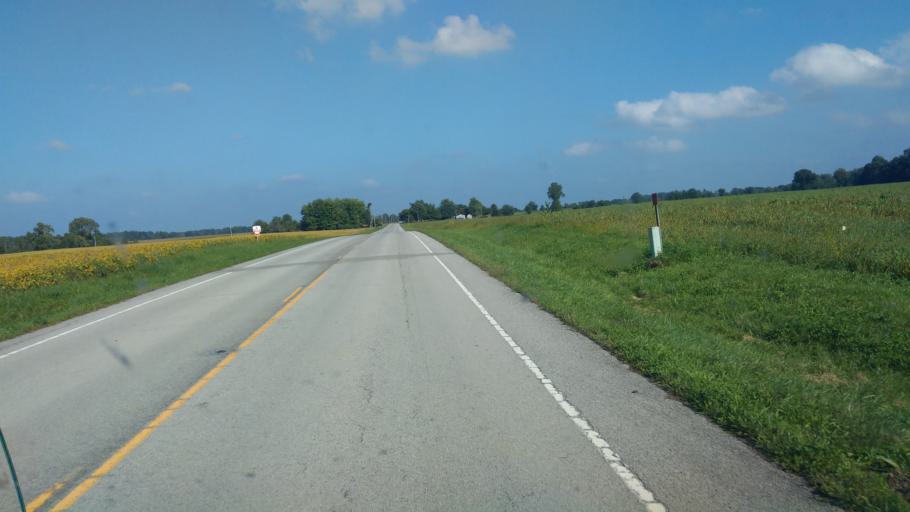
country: US
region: Ohio
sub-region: Hancock County
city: Arlington
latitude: 40.8341
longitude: -83.6967
